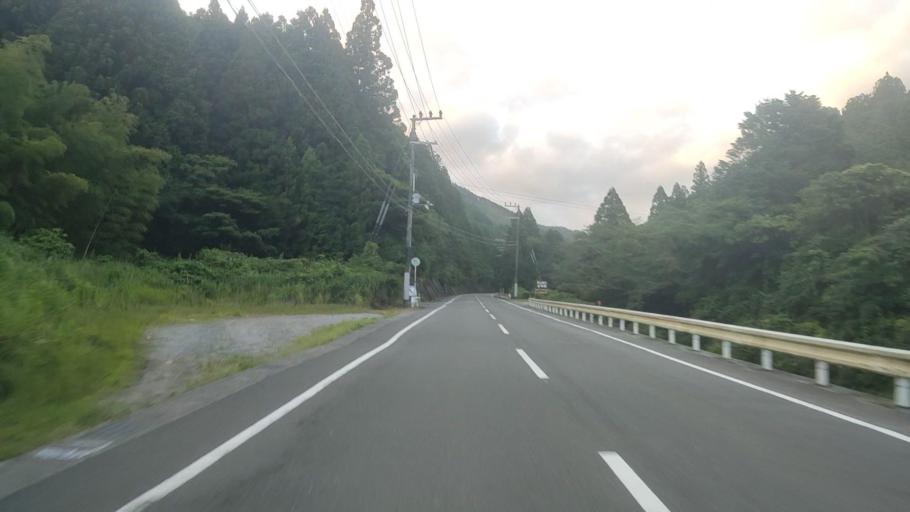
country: JP
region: Wakayama
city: Tanabe
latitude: 33.8278
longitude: 135.6395
